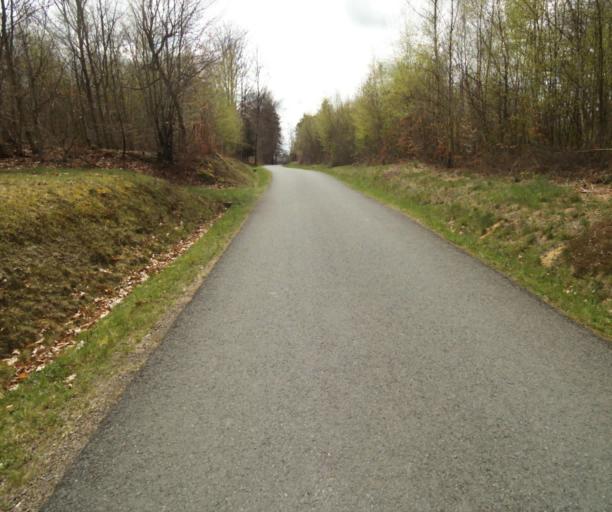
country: FR
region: Limousin
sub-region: Departement de la Correze
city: Laguenne
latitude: 45.2041
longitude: 1.8895
